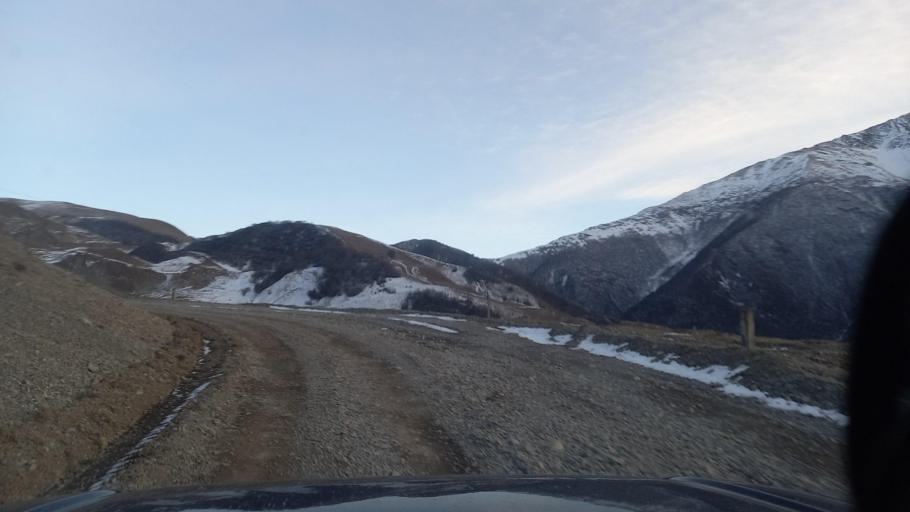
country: RU
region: Ingushetiya
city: Dzhayrakh
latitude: 42.8393
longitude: 44.5435
